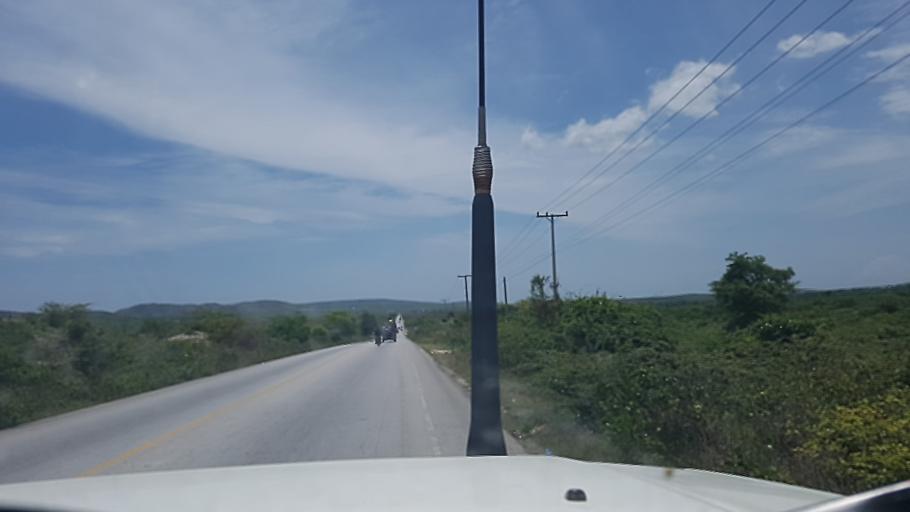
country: HT
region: Artibonite
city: Saint-Marc
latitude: 19.1521
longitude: -72.6348
